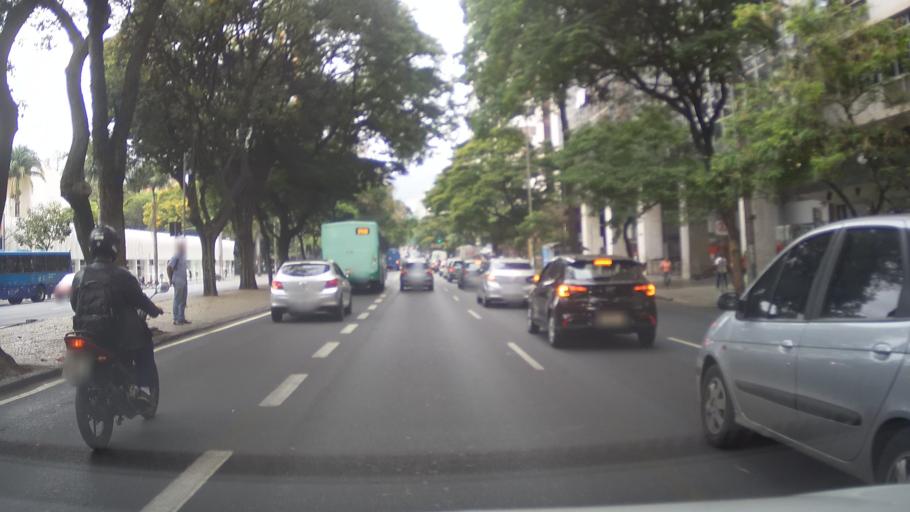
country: BR
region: Minas Gerais
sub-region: Belo Horizonte
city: Belo Horizonte
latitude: -19.9251
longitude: -43.9350
